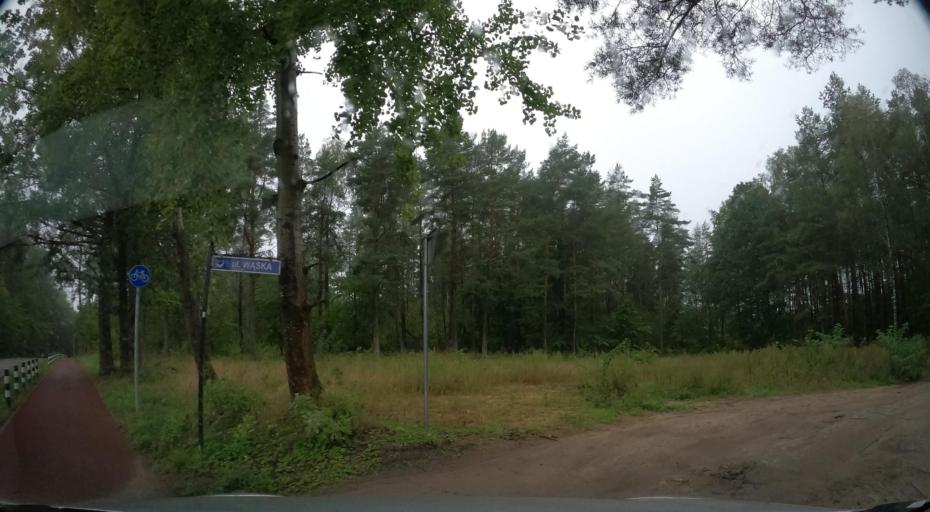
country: PL
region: Pomeranian Voivodeship
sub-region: Powiat kartuski
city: Chwaszczyno
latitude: 54.4349
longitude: 18.4180
